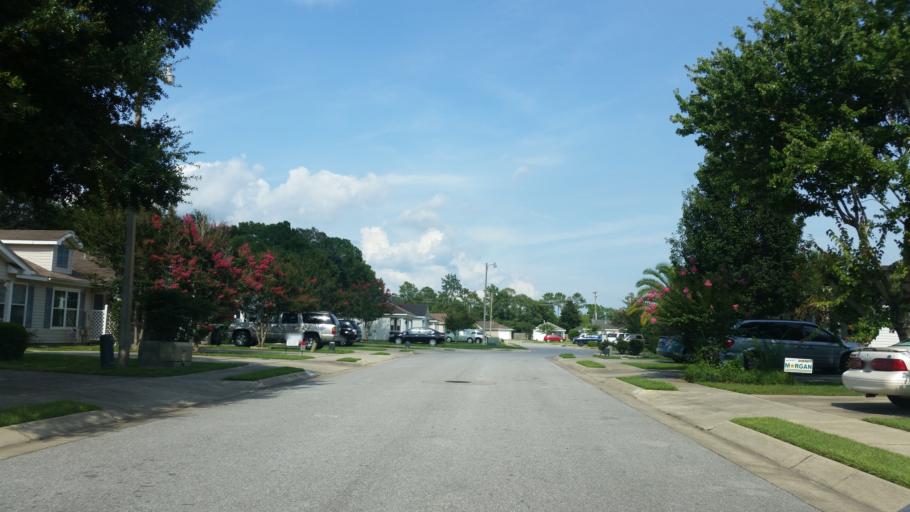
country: US
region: Florida
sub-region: Escambia County
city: Gonzalez
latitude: 30.5411
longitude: -87.3153
